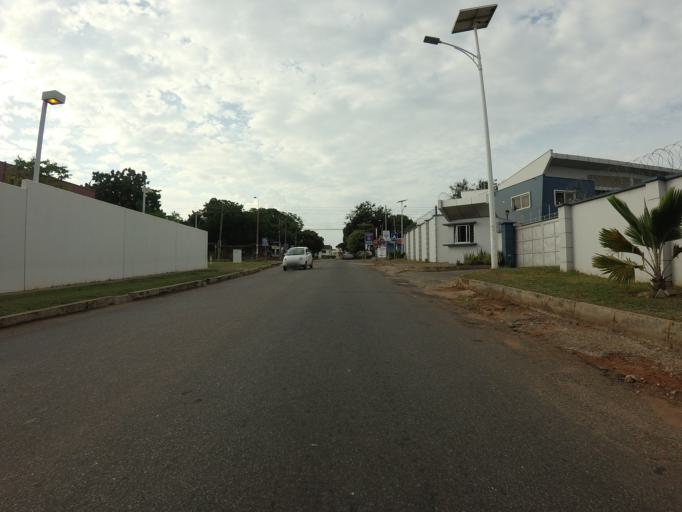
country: GH
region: Greater Accra
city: Accra
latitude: 5.5808
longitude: -0.1705
